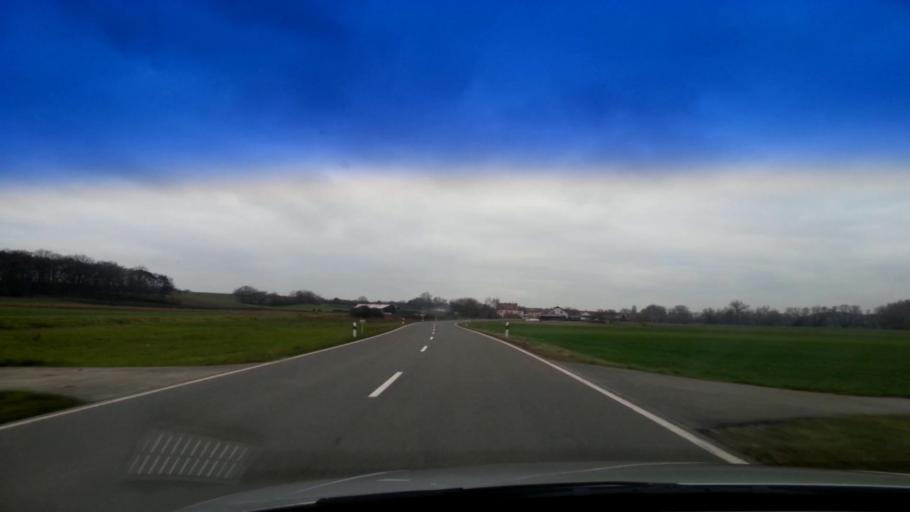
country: DE
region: Bavaria
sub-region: Upper Franconia
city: Walsdorf
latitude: 49.8204
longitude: 10.7915
